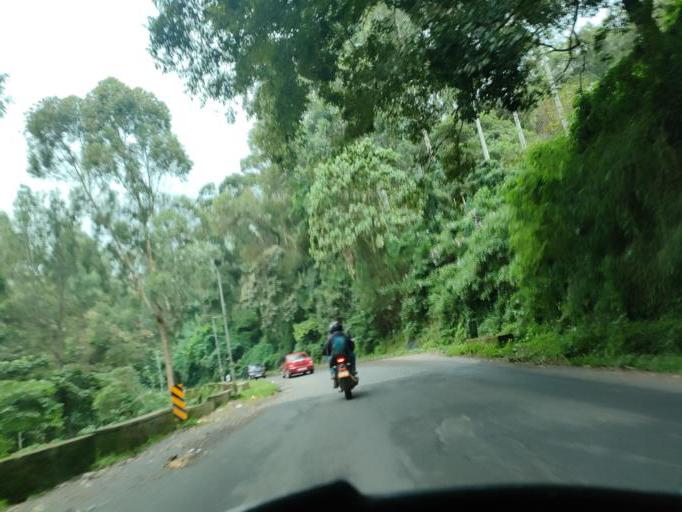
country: IN
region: Tamil Nadu
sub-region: Dindigul
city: Kodaikanal
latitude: 10.2297
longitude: 77.5011
